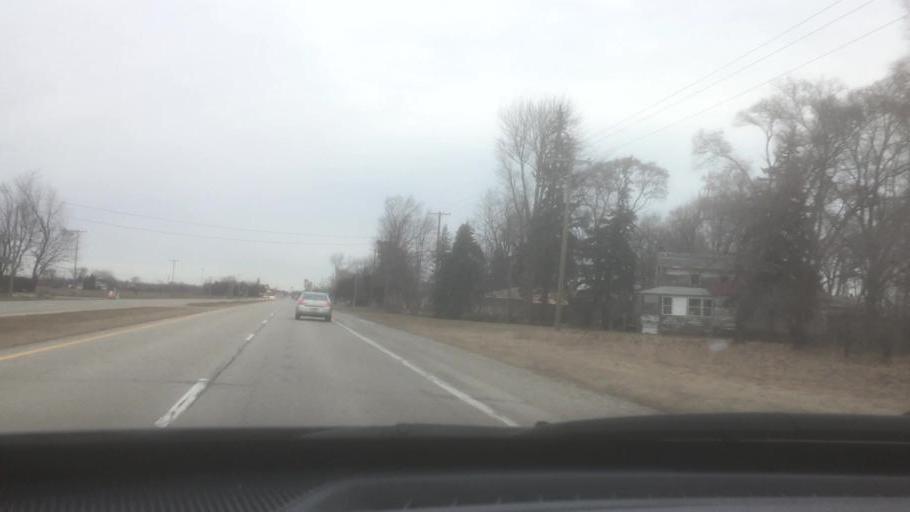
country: US
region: Michigan
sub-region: Bay County
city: Essexville
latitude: 43.5619
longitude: -83.8411
